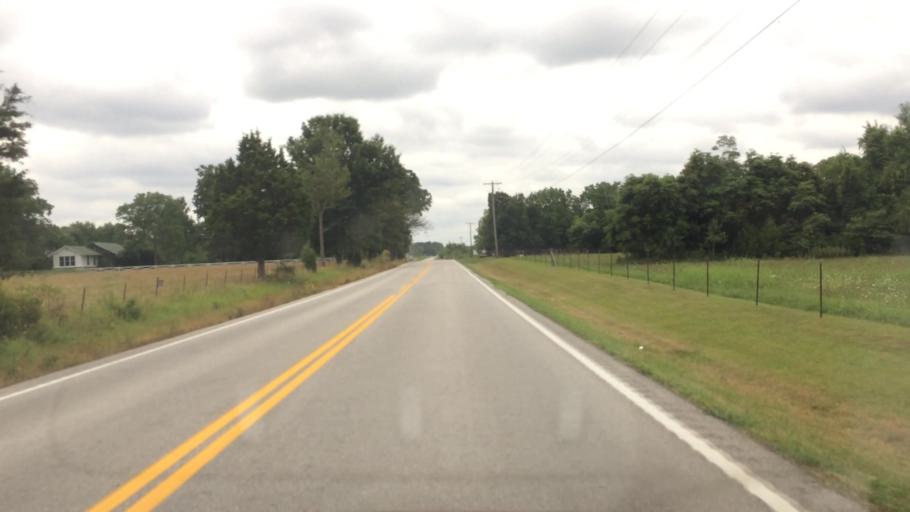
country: US
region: Missouri
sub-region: Greene County
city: Strafford
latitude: 37.2901
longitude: -93.1131
